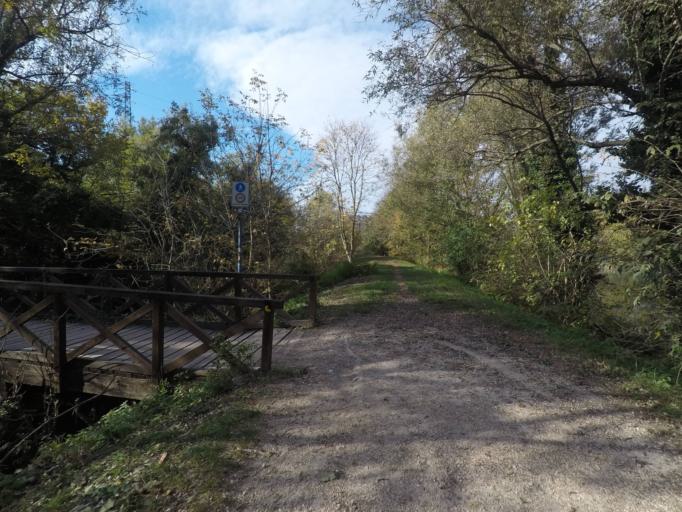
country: IT
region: Veneto
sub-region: Provincia di Treviso
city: Casier
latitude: 45.6473
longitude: 12.2958
